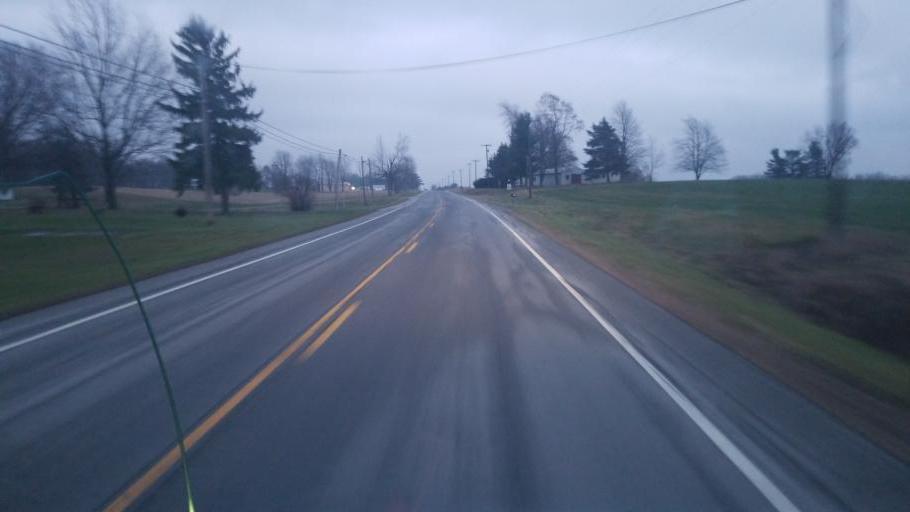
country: US
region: Ohio
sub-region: Crawford County
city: Bucyrus
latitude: 40.8384
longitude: -83.0752
